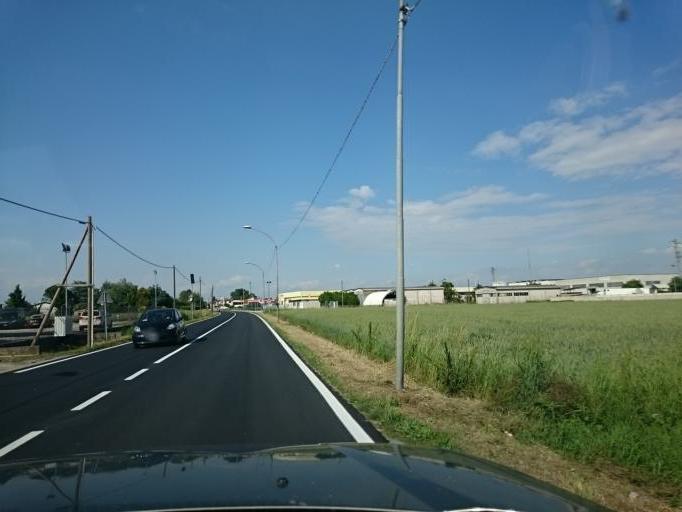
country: IT
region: Veneto
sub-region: Provincia di Vicenza
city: Montegalda
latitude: 45.4593
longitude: 11.6914
